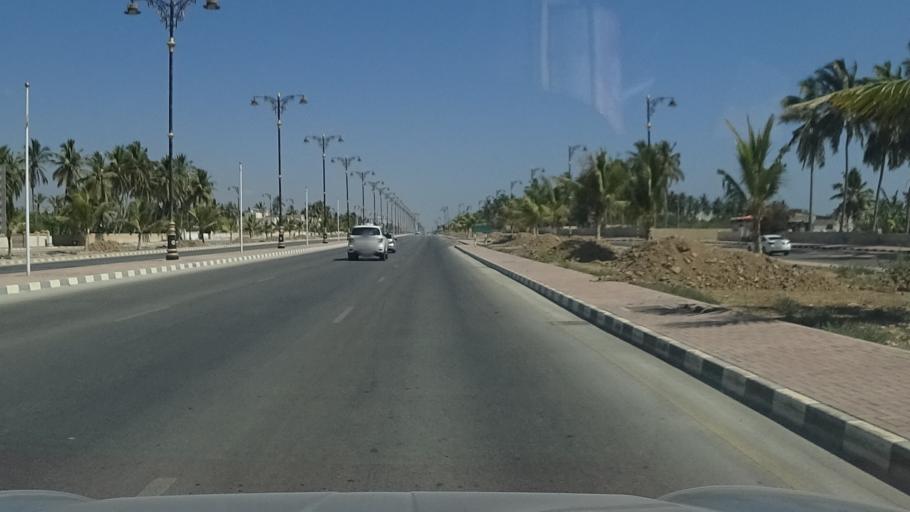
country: OM
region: Zufar
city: Salalah
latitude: 17.0368
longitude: 54.1525
